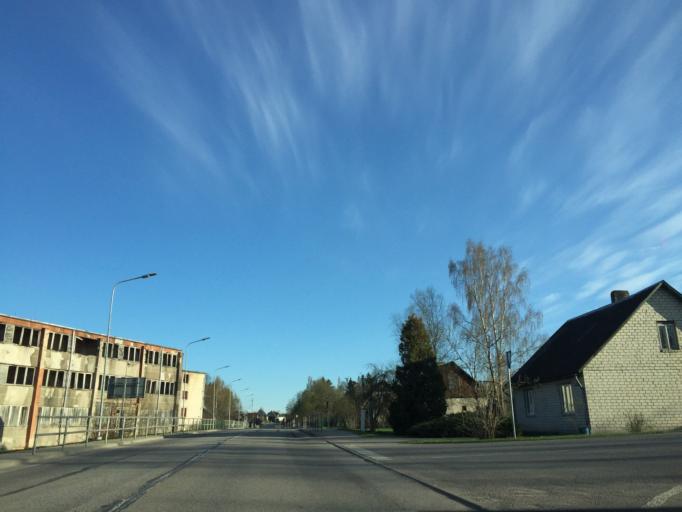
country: LV
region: Valkas Rajons
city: Valka
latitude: 57.7800
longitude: 25.9918
